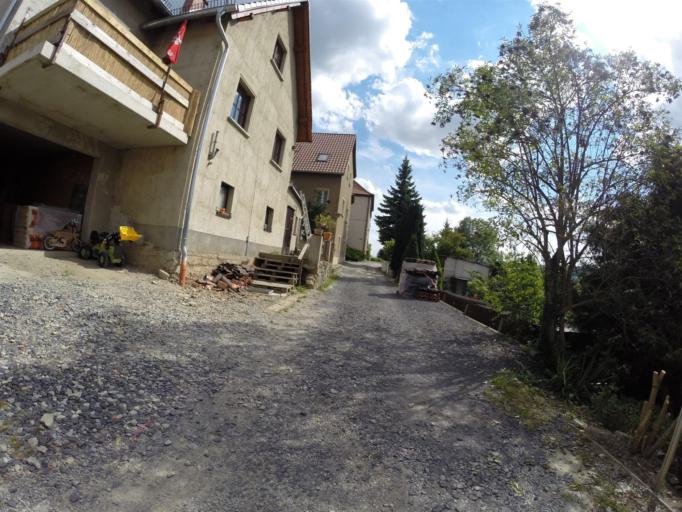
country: DE
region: Thuringia
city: Jena
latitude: 50.9111
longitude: 11.5889
